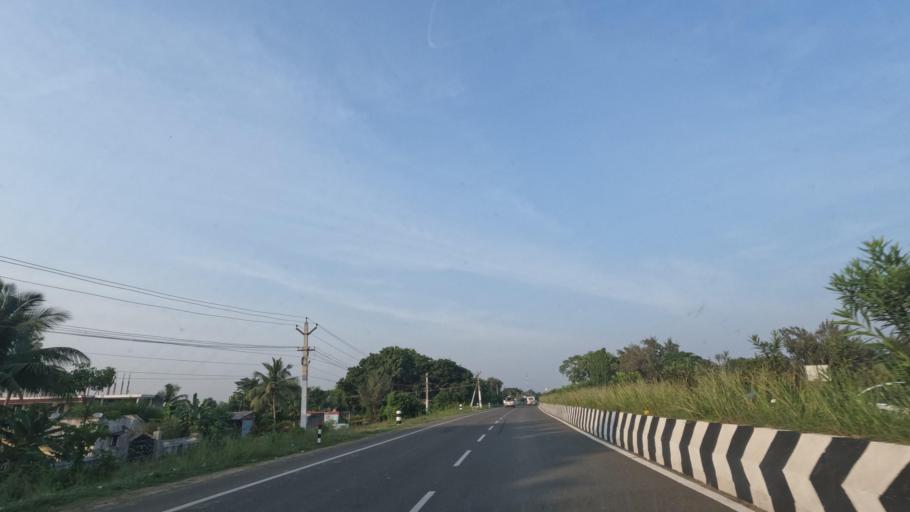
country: IN
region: Tamil Nadu
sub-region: Kancheepuram
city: Mamallapuram
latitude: 12.6440
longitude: 80.2007
